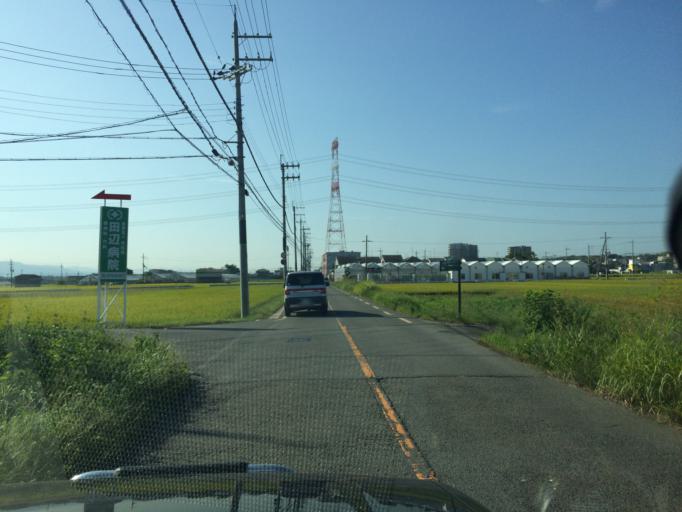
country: JP
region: Kyoto
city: Tanabe
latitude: 34.8054
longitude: 135.7887
